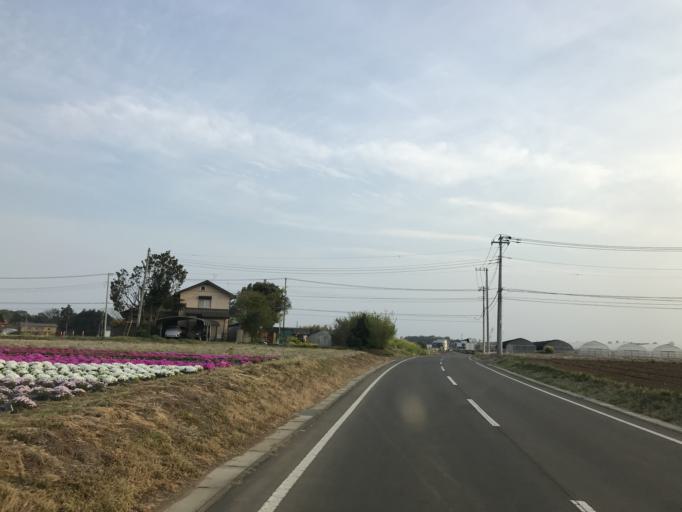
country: JP
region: Ibaraki
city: Tsukuba
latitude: 36.1232
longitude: 140.0838
